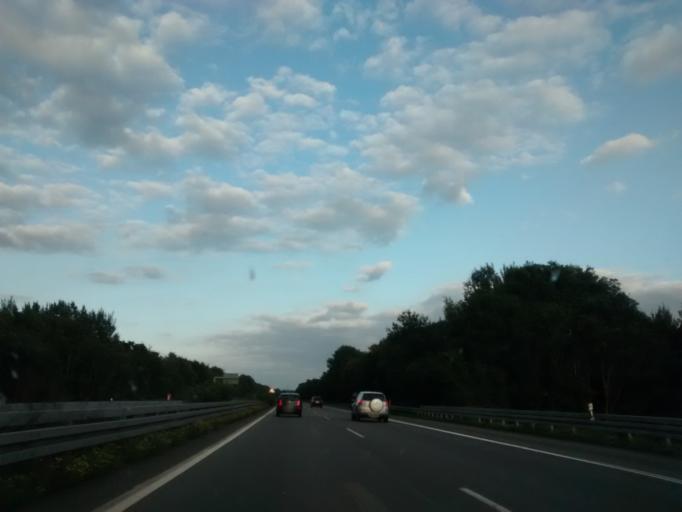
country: DE
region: North Rhine-Westphalia
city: Ibbenburen
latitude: 52.2576
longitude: 7.7316
